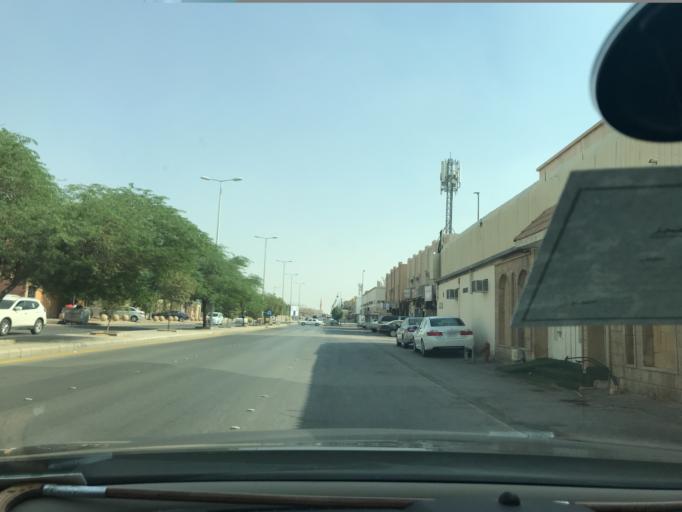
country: SA
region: Ar Riyad
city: Riyadh
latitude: 24.7446
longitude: 46.7643
